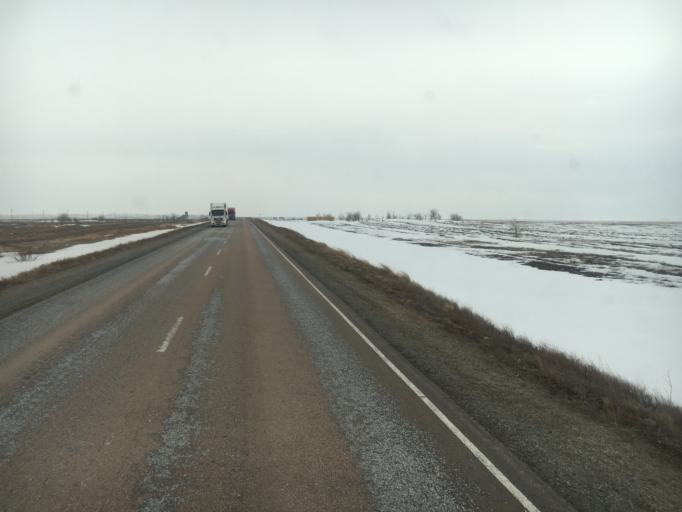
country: RU
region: Orenburg
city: Dombarovskiy
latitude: 50.0939
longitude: 59.4875
